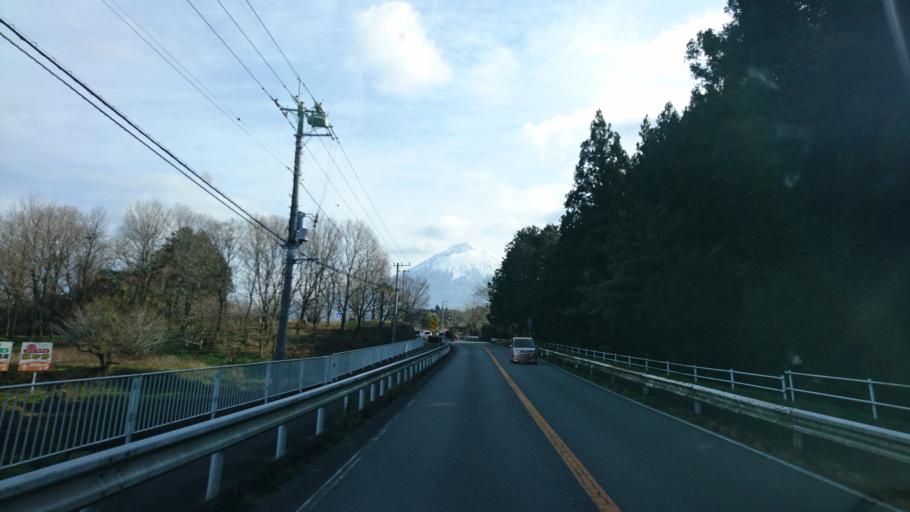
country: JP
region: Shizuoka
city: Fujinomiya
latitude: 35.2742
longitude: 138.6035
